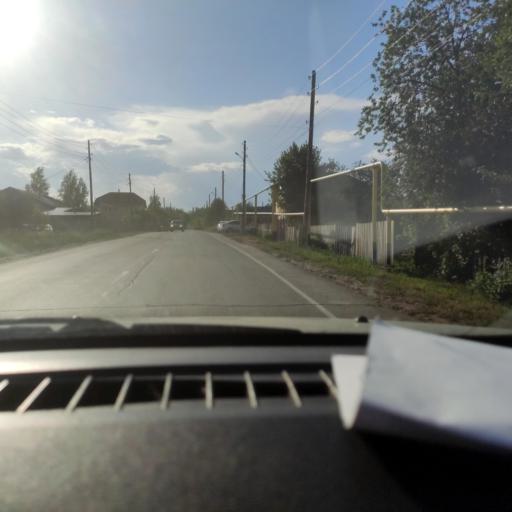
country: RU
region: Perm
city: Krasnokamsk
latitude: 58.1420
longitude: 55.7357
